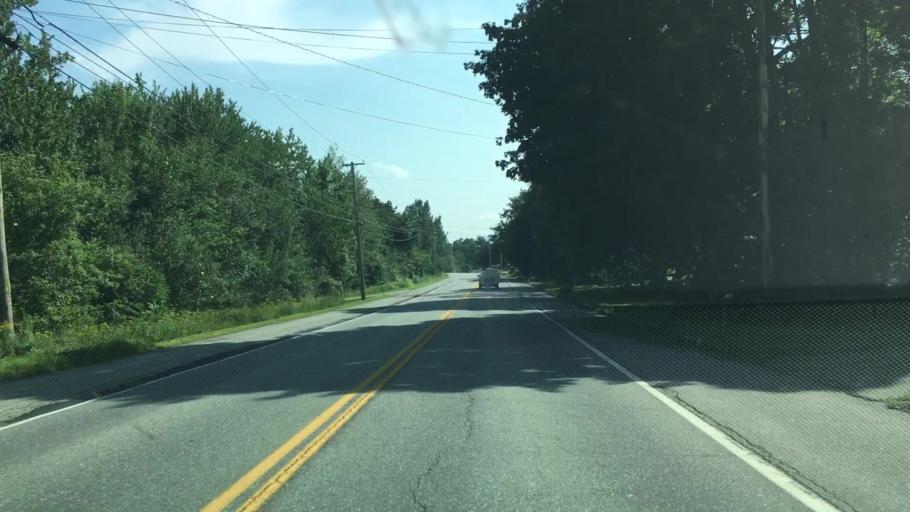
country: US
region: Maine
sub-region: Penobscot County
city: Orrington
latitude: 44.7167
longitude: -68.8456
